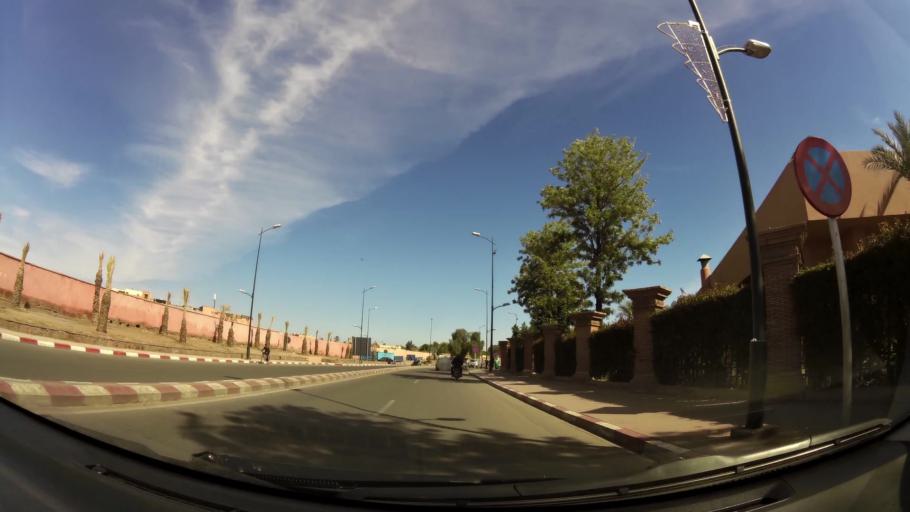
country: MA
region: Marrakech-Tensift-Al Haouz
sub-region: Marrakech
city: Marrakesh
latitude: 31.6424
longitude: -7.9856
